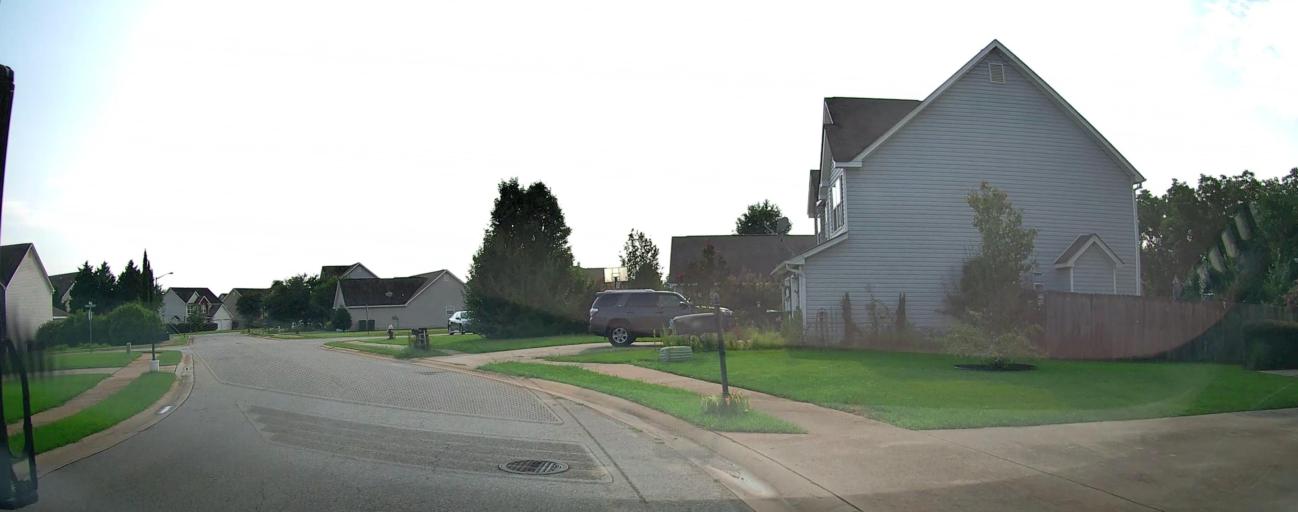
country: US
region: Georgia
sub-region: Houston County
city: Centerville
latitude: 32.6311
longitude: -83.7147
